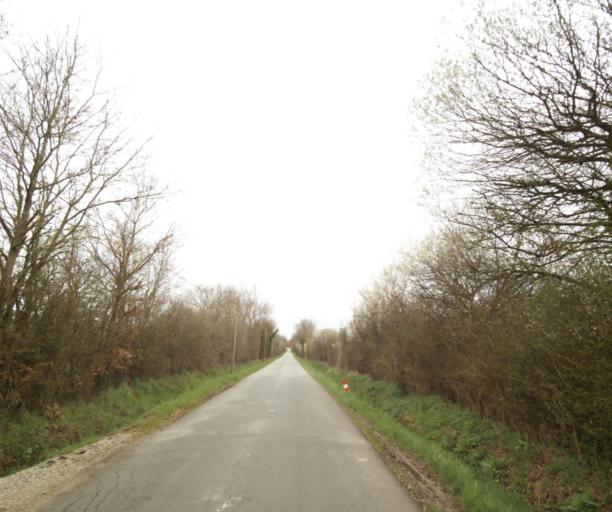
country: FR
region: Pays de la Loire
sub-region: Departement de la Loire-Atlantique
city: Bouvron
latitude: 47.4348
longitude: -1.8903
